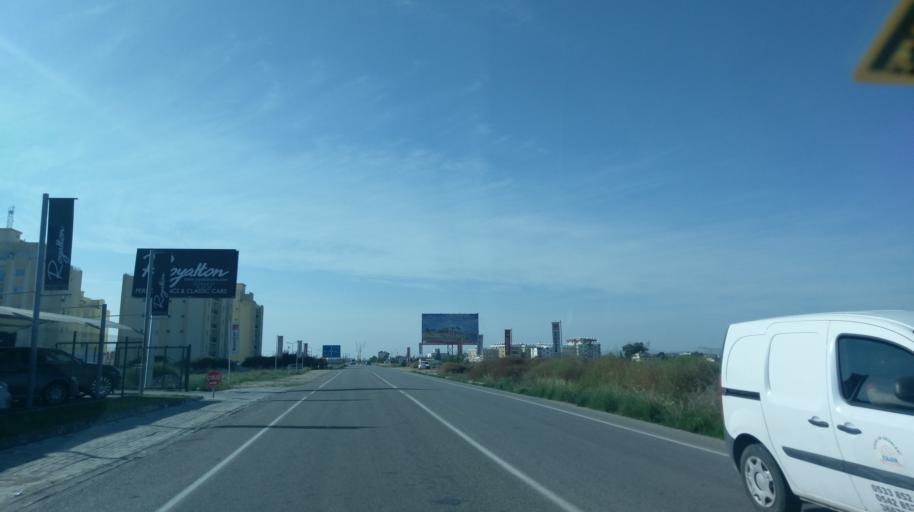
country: CY
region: Ammochostos
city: Trikomo
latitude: 35.2788
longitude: 33.9029
